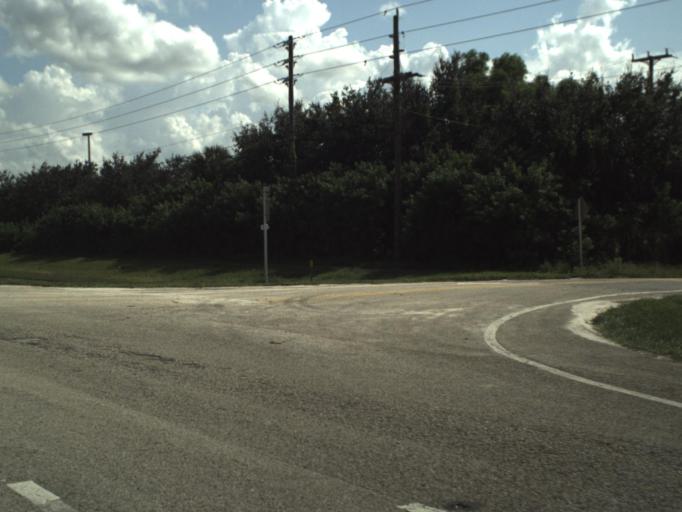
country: US
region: Florida
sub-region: Palm Beach County
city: Villages of Oriole
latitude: 26.4707
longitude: -80.2048
